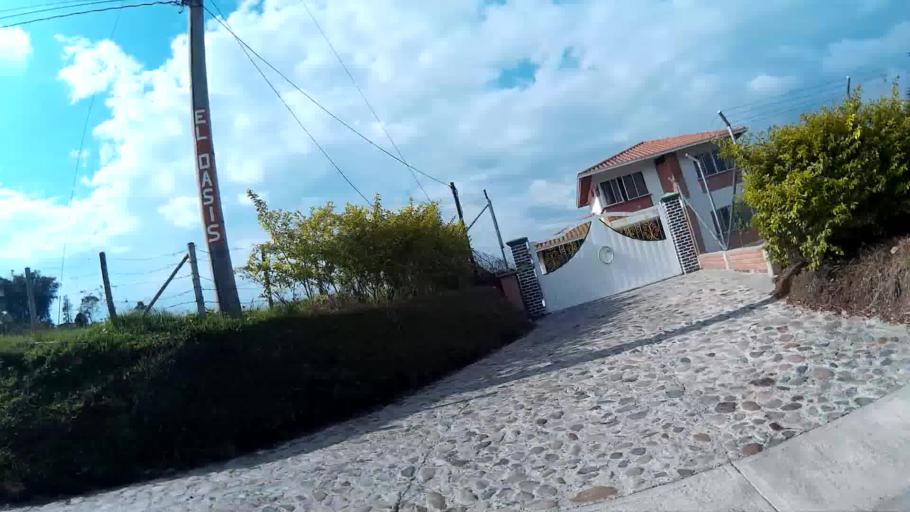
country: CO
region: Quindio
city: Filandia
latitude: 4.6765
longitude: -75.6540
